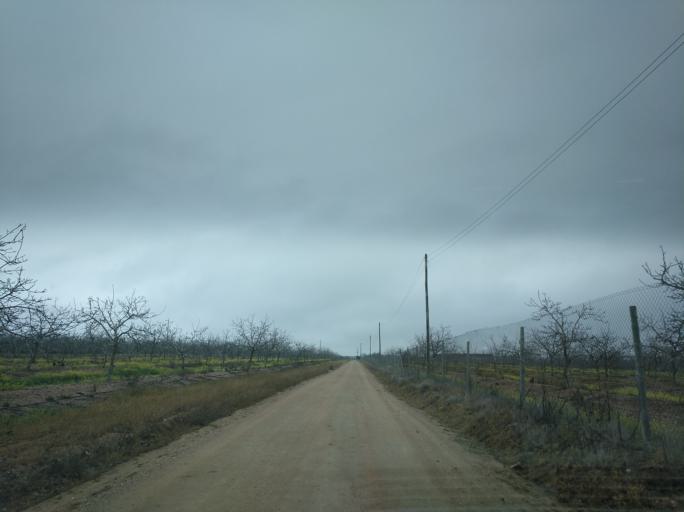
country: PT
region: Portalegre
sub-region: Campo Maior
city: Campo Maior
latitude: 38.9556
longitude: -7.0514
